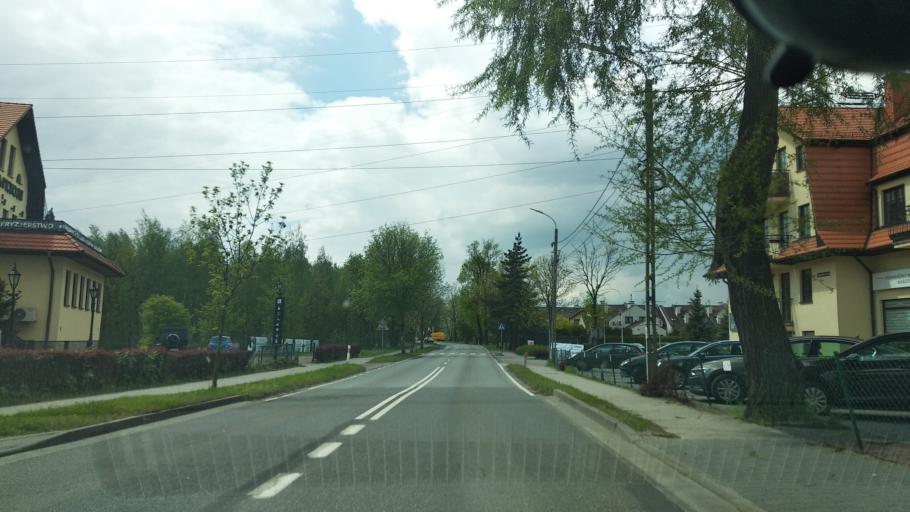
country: PL
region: Silesian Voivodeship
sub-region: Powiat mikolowski
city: Mikolow
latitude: 50.2298
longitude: 18.9428
